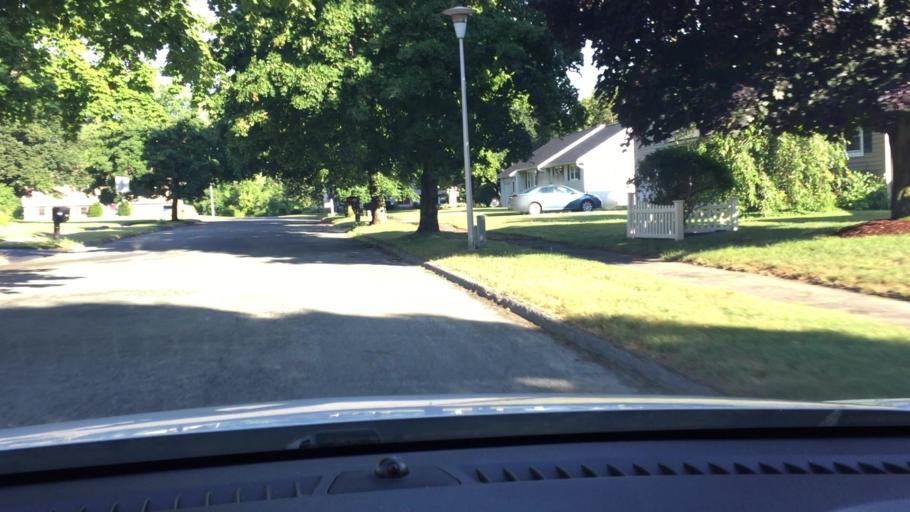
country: US
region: Massachusetts
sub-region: Berkshire County
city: Pittsfield
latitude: 42.4182
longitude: -73.2338
